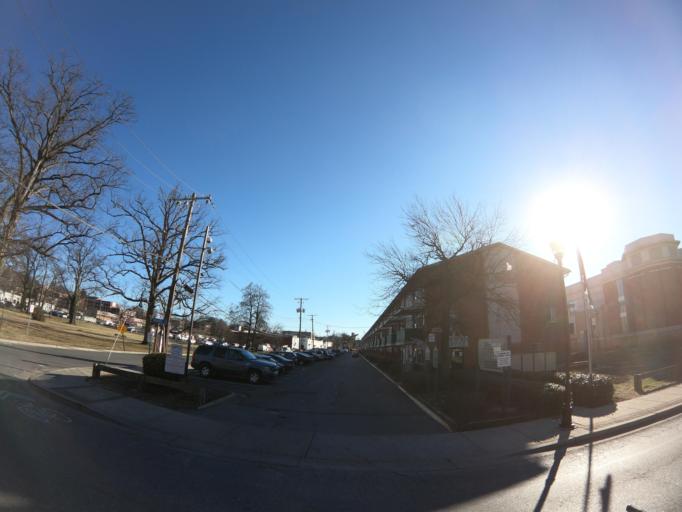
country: US
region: Maryland
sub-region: Prince George's County
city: East Riverdale
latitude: 38.9593
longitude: -76.9220
